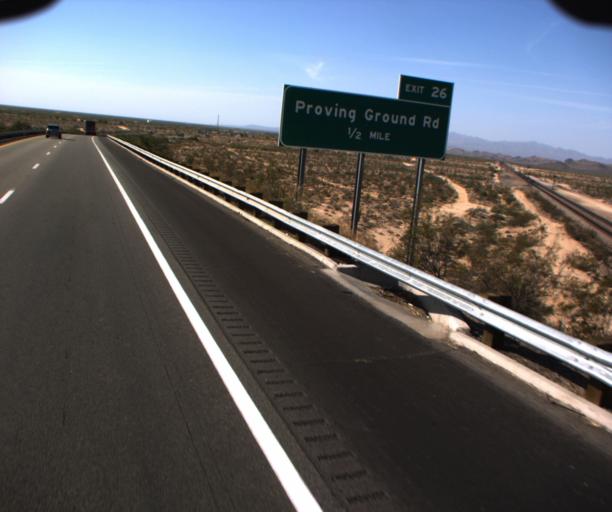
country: US
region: Arizona
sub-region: Mohave County
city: Kingman
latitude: 34.8884
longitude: -114.1515
